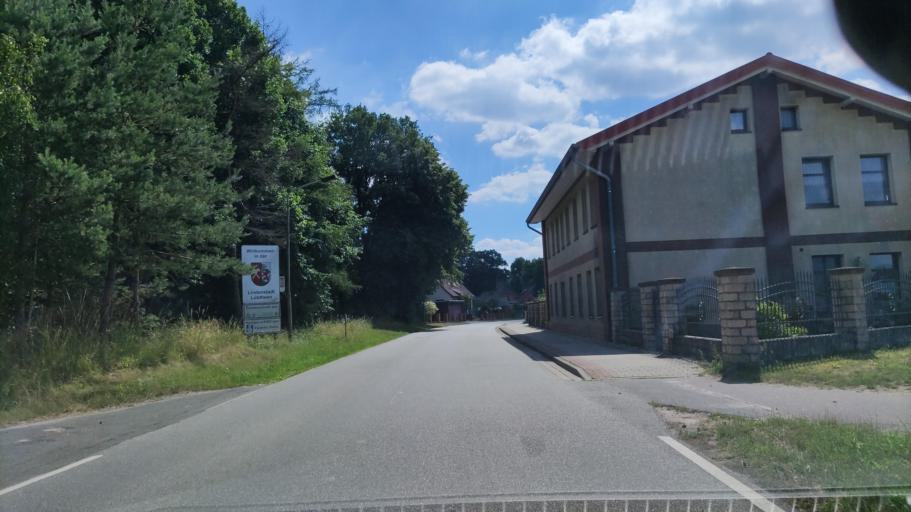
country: DE
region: Mecklenburg-Vorpommern
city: Lubtheen
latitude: 53.3084
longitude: 11.0874
